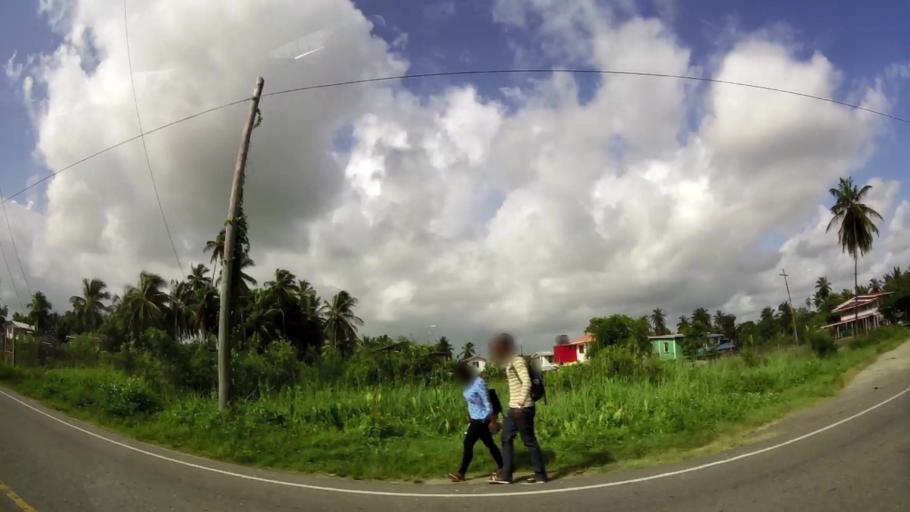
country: GY
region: Demerara-Mahaica
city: Mahaica Village
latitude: 6.6773
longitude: -57.9221
